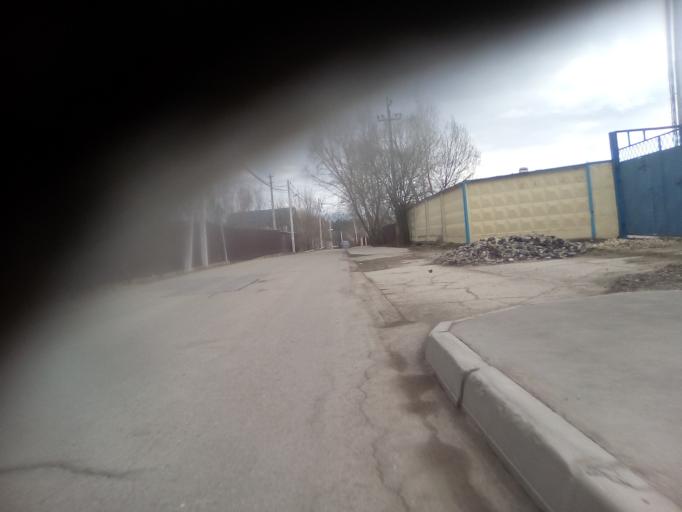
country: RU
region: Moskovskaya
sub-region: Leninskiy Rayon
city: Vnukovo
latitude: 55.5920
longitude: 37.3204
